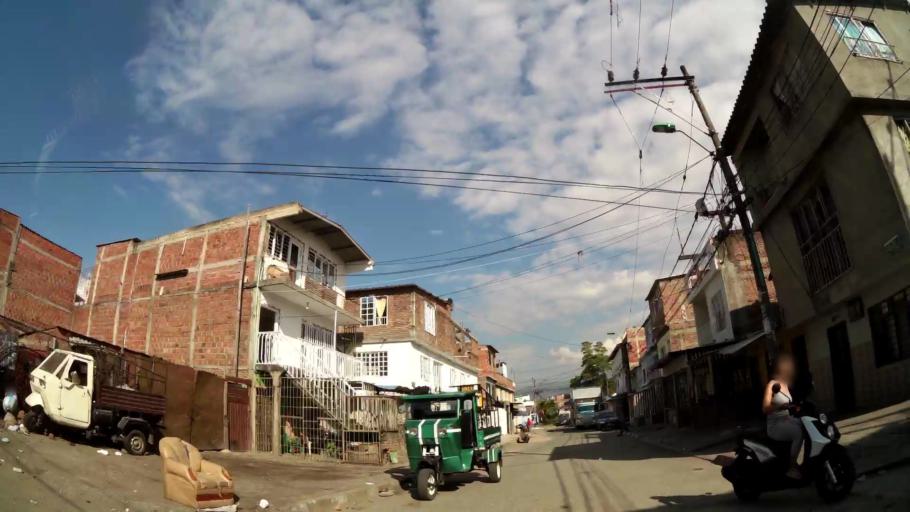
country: CO
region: Valle del Cauca
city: Cali
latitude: 3.4239
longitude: -76.5044
